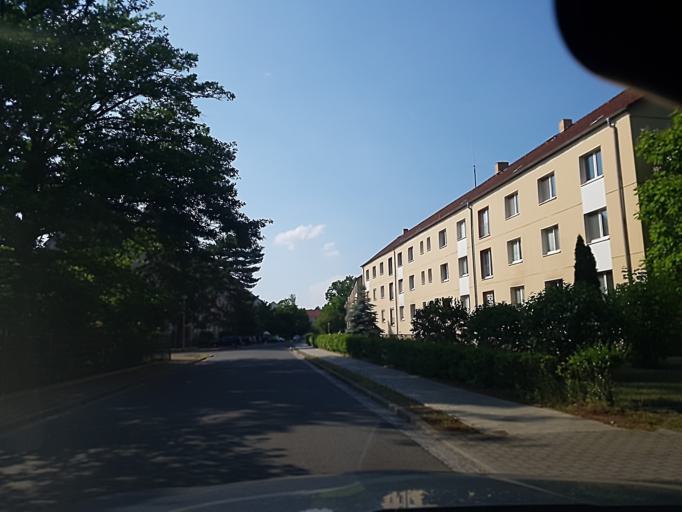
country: DE
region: Brandenburg
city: Bad Liebenwerda
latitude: 51.5254
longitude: 13.4041
